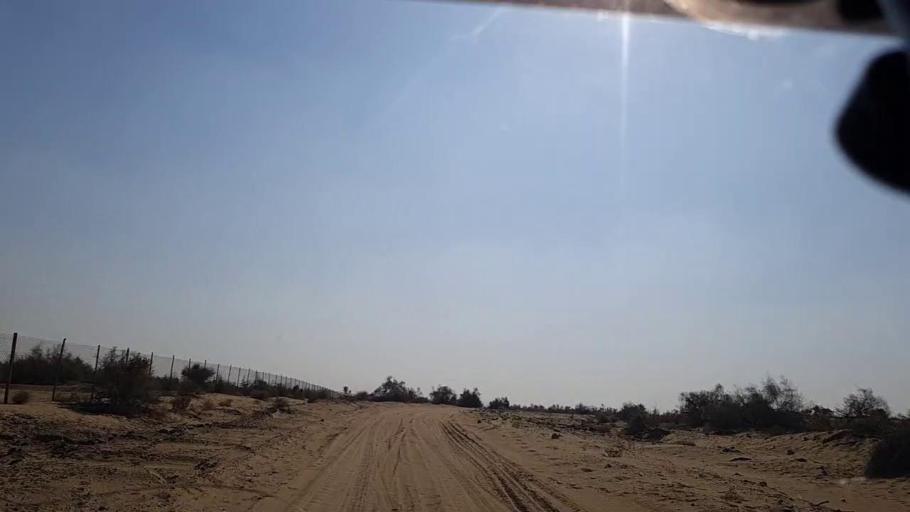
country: PK
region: Sindh
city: Khanpur
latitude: 27.5606
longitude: 69.3885
